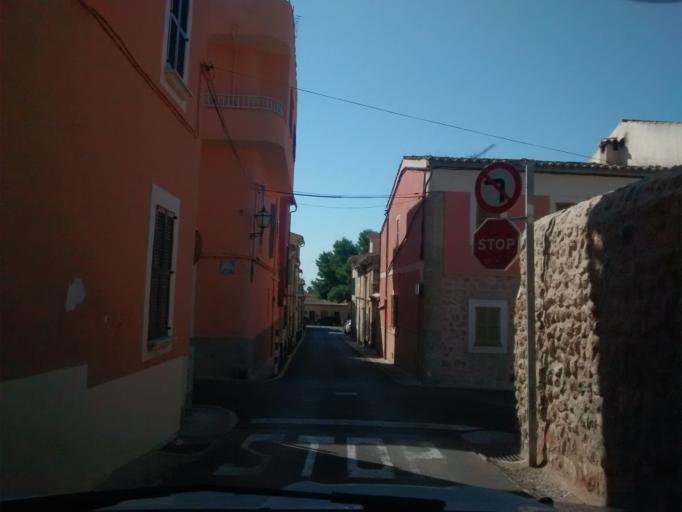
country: ES
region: Balearic Islands
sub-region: Illes Balears
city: Alaro
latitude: 39.7042
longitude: 2.7893
